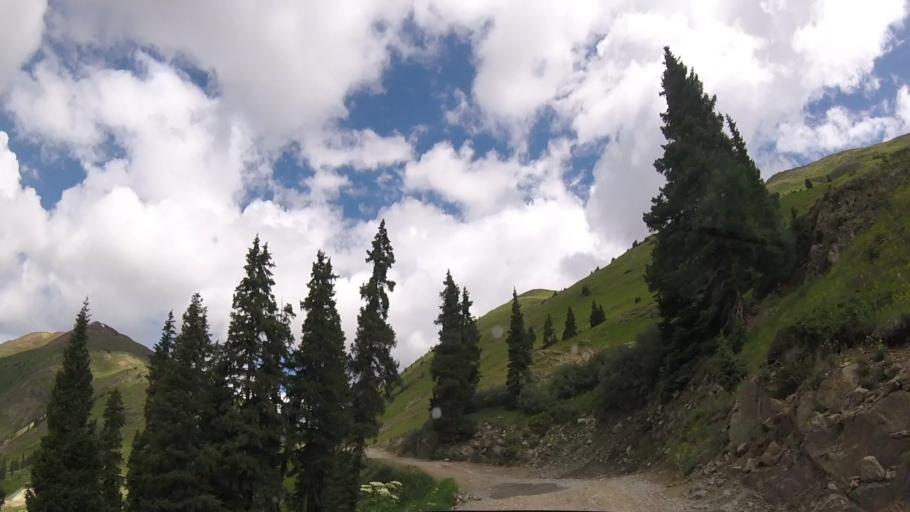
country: US
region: Colorado
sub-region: Ouray County
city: Ouray
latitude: 37.9315
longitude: -107.5672
